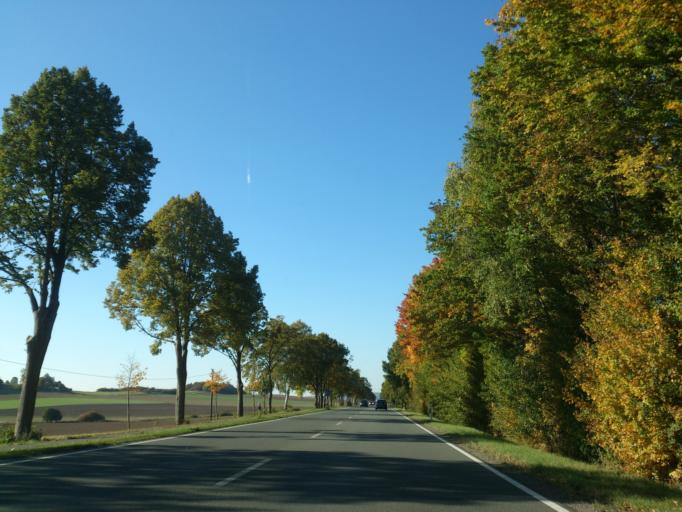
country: DE
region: North Rhine-Westphalia
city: Warburg
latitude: 51.5007
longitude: 9.1108
